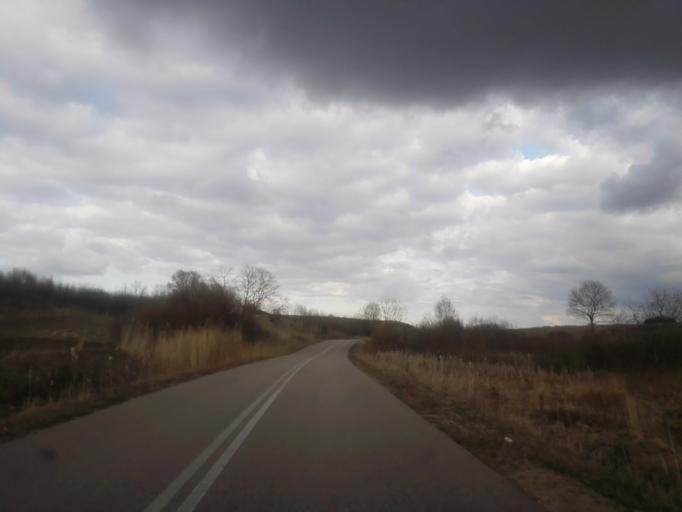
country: PL
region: Podlasie
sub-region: Suwalki
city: Suwalki
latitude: 54.1997
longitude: 22.9772
